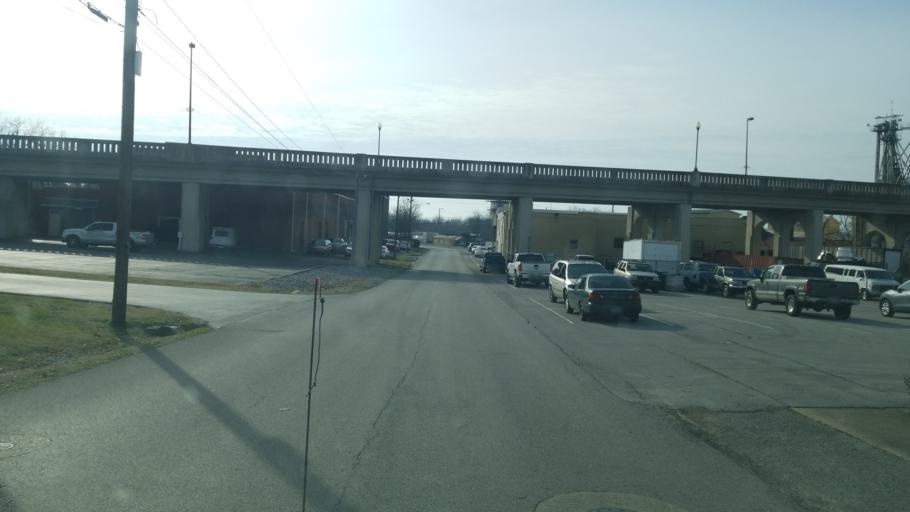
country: US
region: Kentucky
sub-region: Boyle County
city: Danville
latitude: 37.6466
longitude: -84.7848
